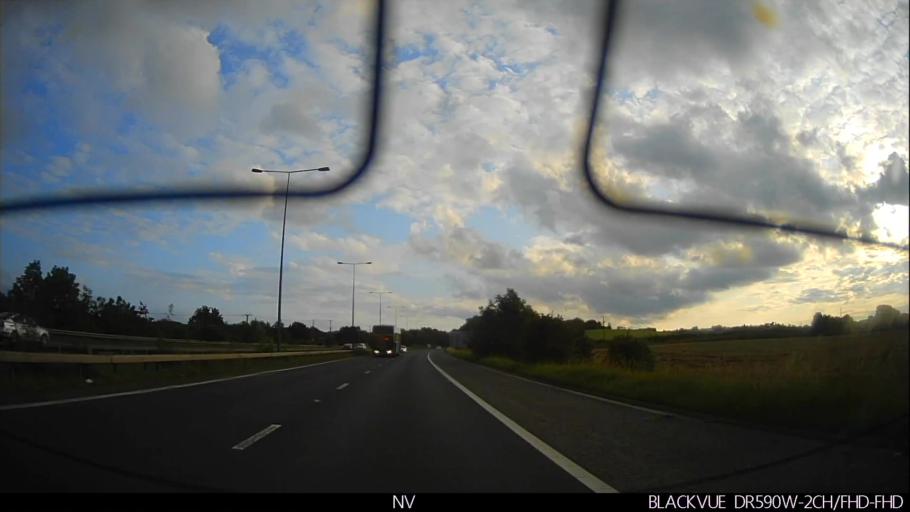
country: GB
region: England
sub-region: City and Borough of Leeds
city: Morley
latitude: 53.7633
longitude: -1.5978
